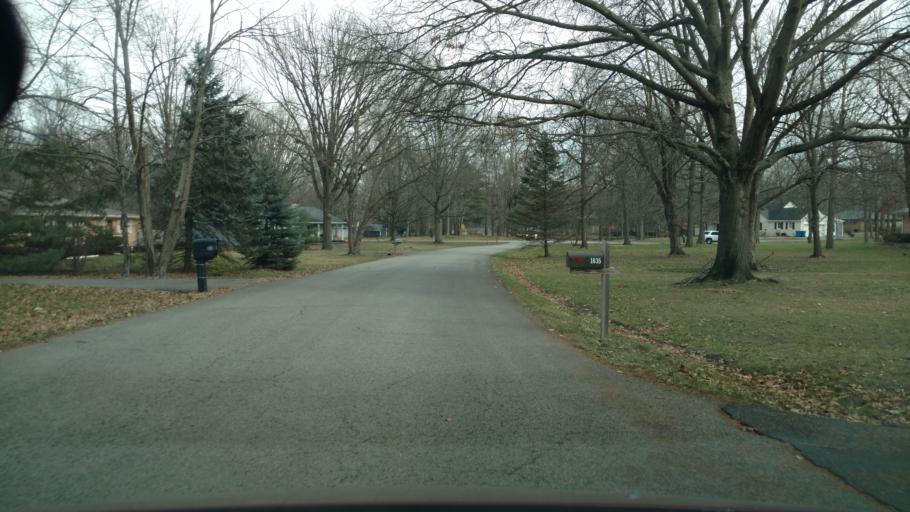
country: US
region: Indiana
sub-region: Marion County
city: Meridian Hills
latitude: 39.9220
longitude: -86.1315
